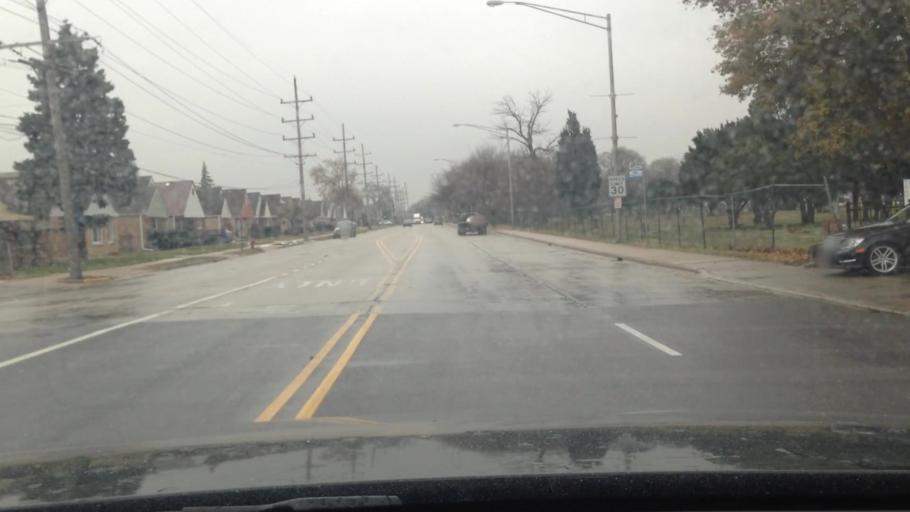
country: US
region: Illinois
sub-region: Cook County
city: Schiller Park
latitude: 41.9552
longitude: -87.8711
